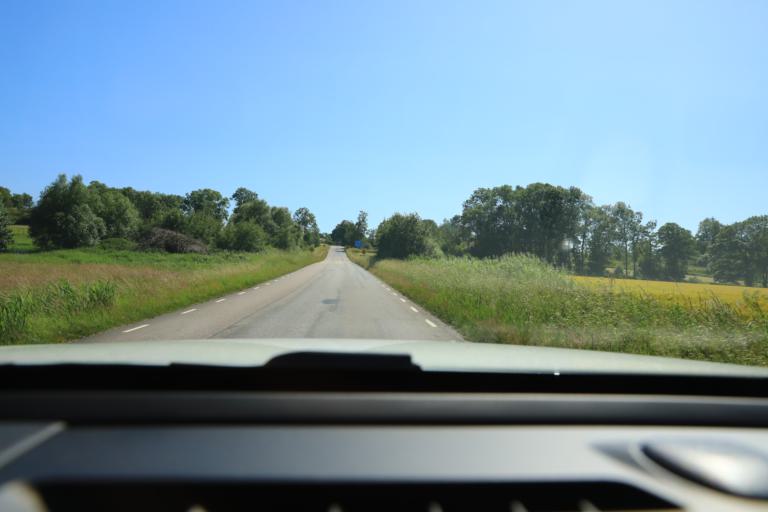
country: SE
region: Halland
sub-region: Varbergs Kommun
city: Varberg
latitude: 57.1620
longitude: 12.3148
